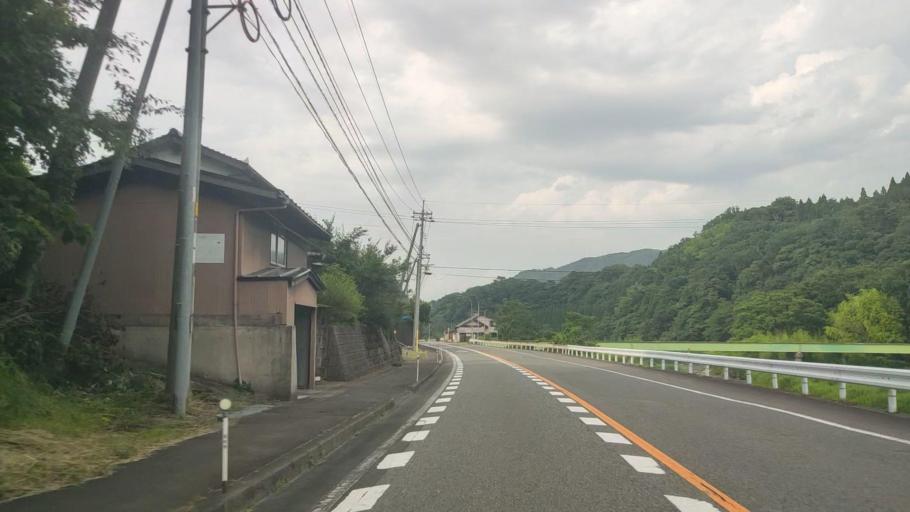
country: JP
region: Tottori
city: Kurayoshi
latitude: 35.3552
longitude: 133.8454
